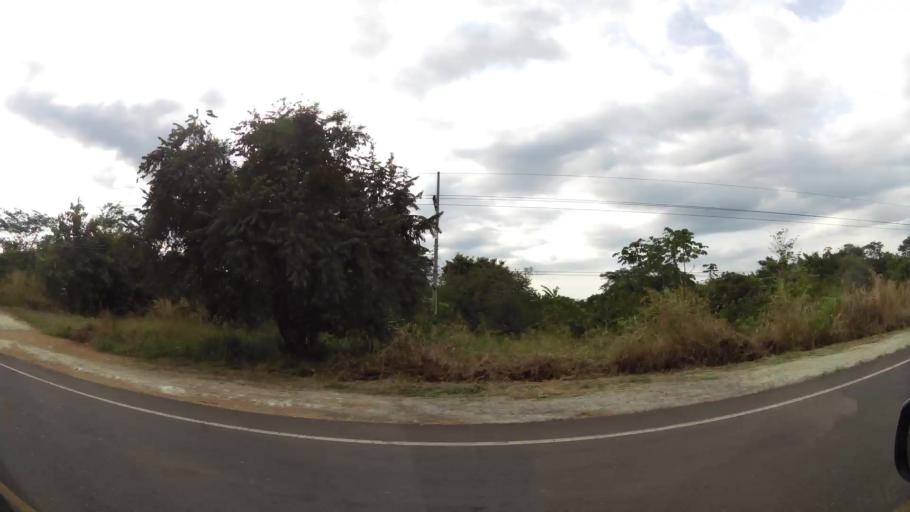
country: CR
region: Alajuela
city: Orotina
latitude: 9.8679
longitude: -84.5735
